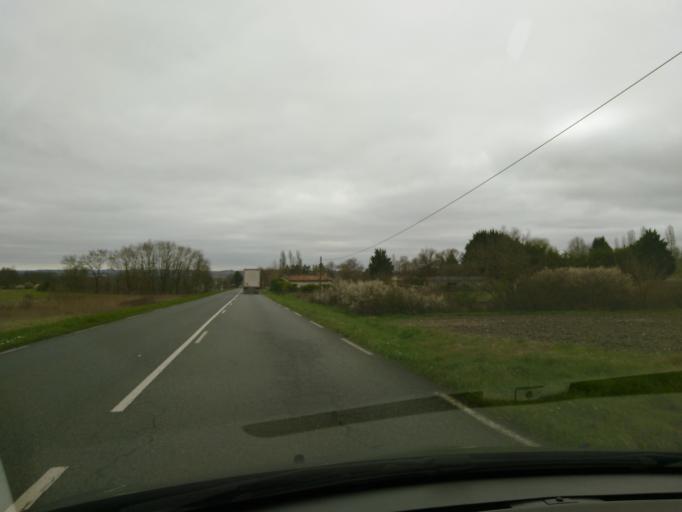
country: FR
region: Aquitaine
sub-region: Departement du Lot-et-Garonne
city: Castillonnes
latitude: 44.6935
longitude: 0.5674
